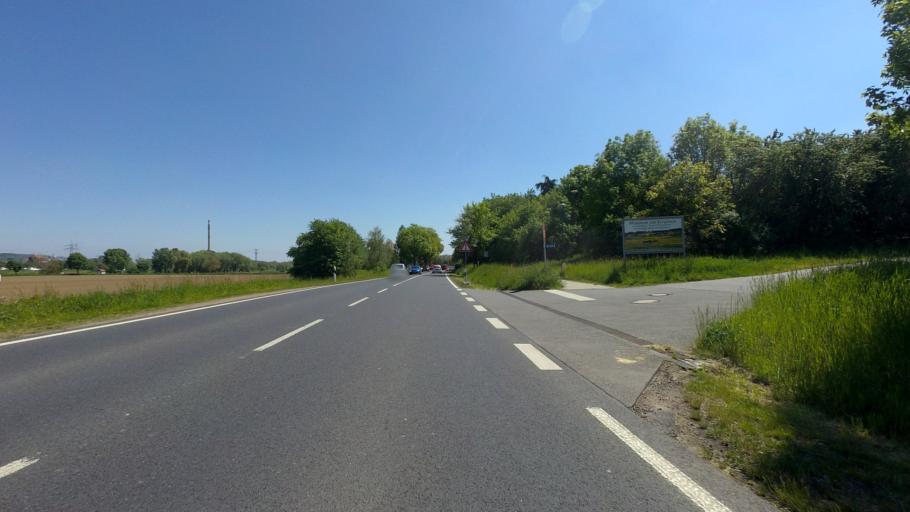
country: DE
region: Saxony
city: Coswig
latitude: 51.1133
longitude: 13.5647
